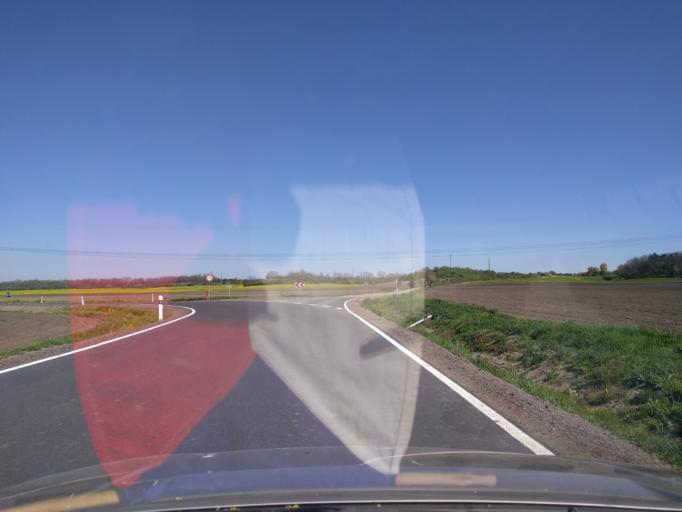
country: CZ
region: Central Bohemia
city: Cesky Brod
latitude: 50.1146
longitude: 14.8616
